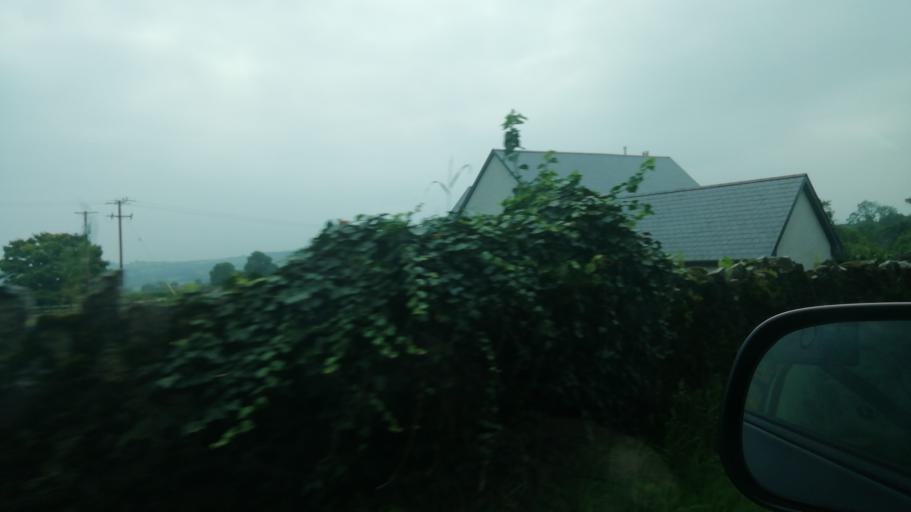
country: IE
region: Munster
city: Fethard
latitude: 52.5518
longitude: -7.6721
